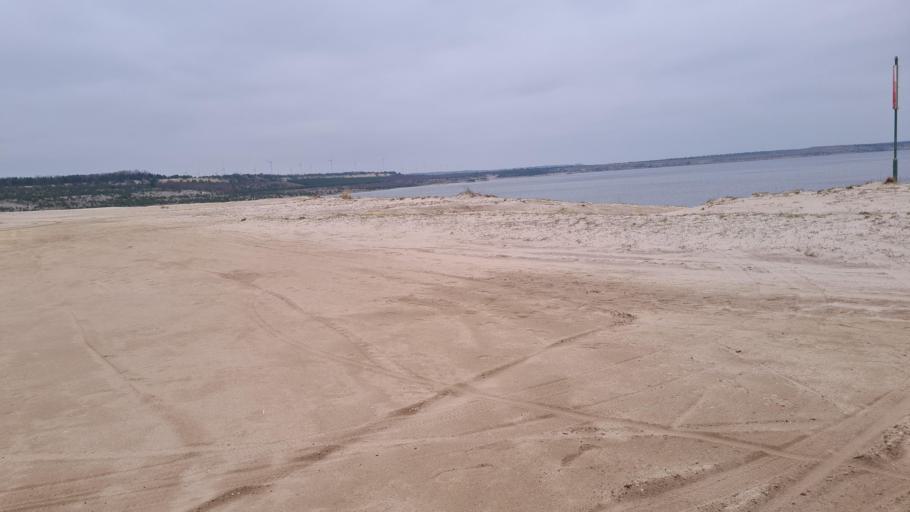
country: DE
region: Brandenburg
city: Sallgast
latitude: 51.5844
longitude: 13.7880
